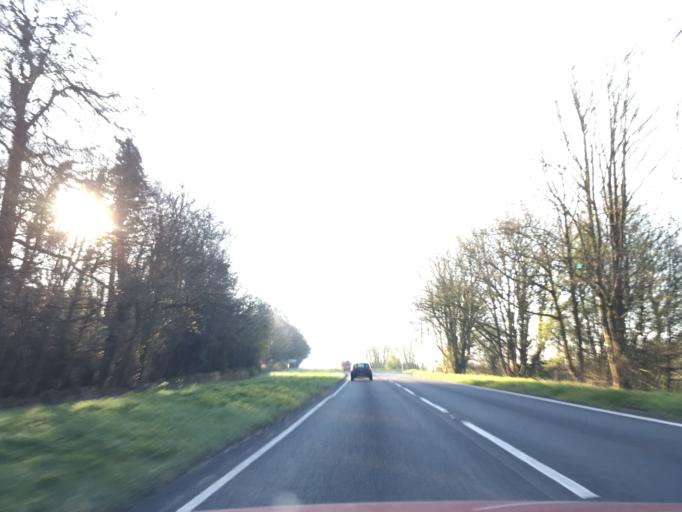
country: GB
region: England
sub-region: Gloucestershire
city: Bourton on the Water
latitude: 51.8173
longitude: -1.7552
